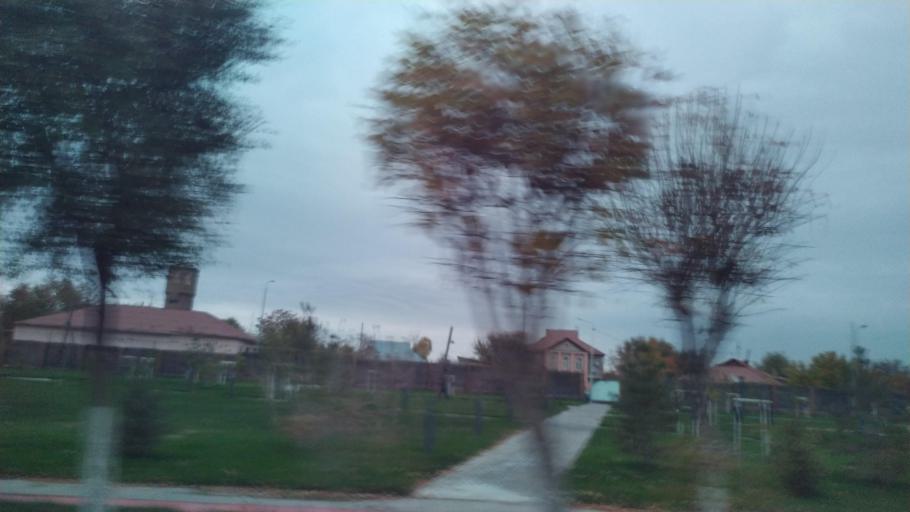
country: KZ
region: Ongtustik Qazaqstan
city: Turkestan
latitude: 43.2984
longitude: 68.2789
